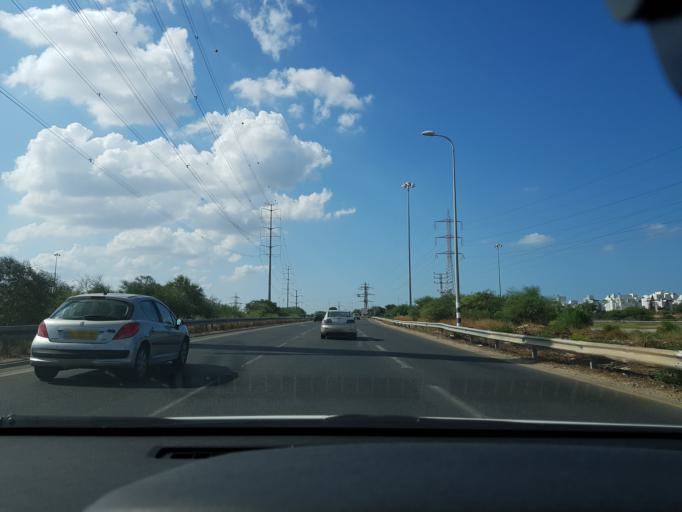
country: IL
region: Central District
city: Rishon LeZiyyon
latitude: 31.9656
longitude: 34.7863
